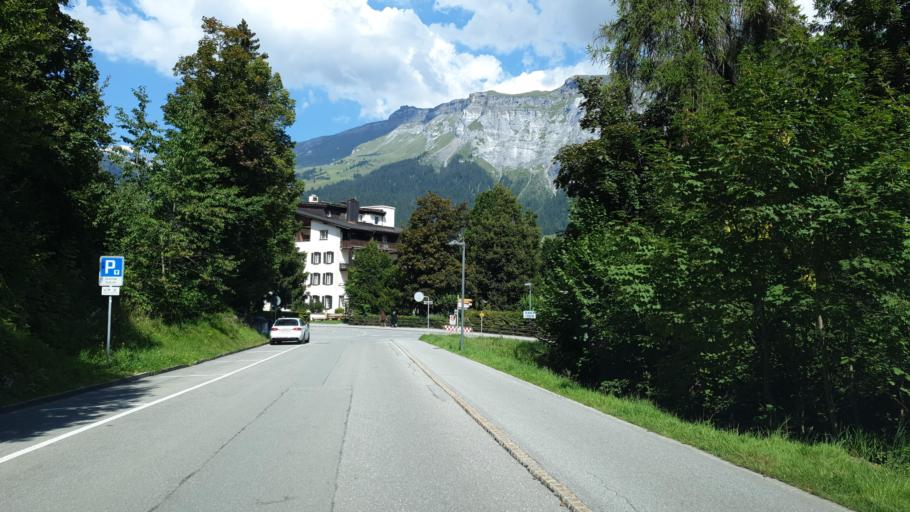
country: CH
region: Grisons
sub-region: Imboden District
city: Flims
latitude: 46.8271
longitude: 9.2907
